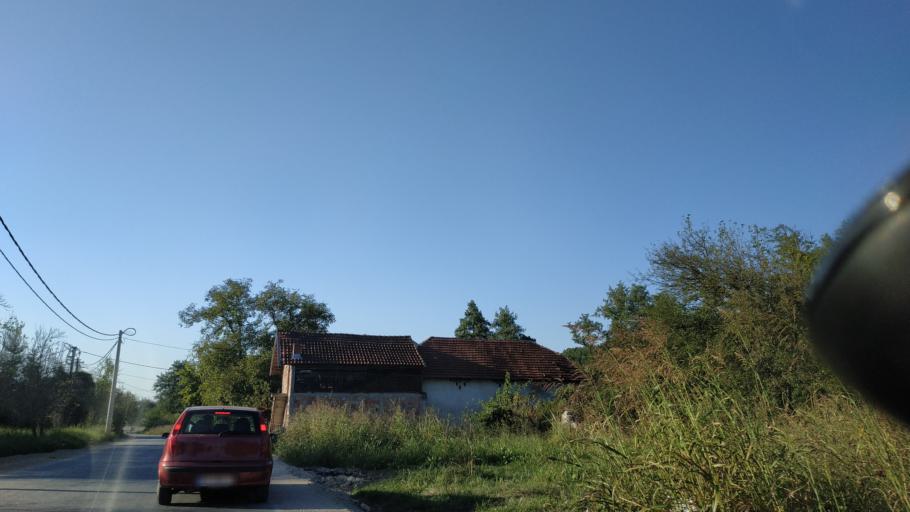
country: RS
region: Central Serbia
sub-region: Rasinski Okrug
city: Krusevac
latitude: 43.4992
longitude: 21.3416
